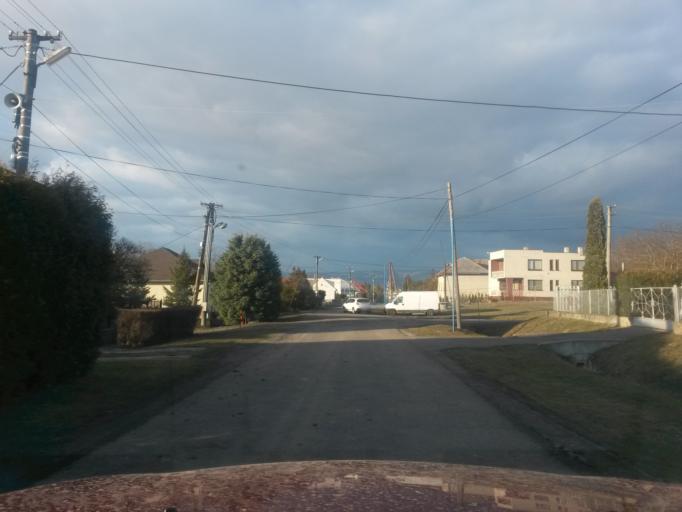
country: SK
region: Kosicky
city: Sobrance
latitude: 48.7339
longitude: 22.0796
